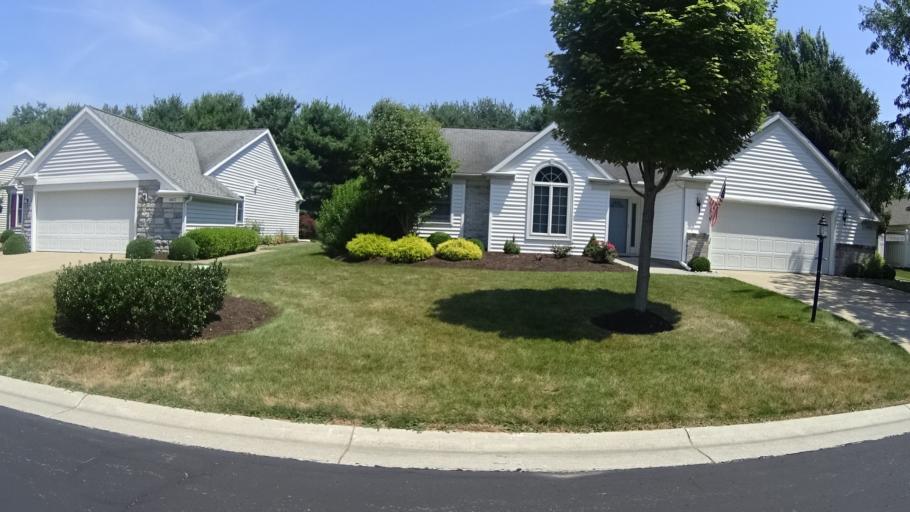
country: US
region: Ohio
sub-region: Erie County
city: Sandusky
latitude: 41.4039
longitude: -82.6512
